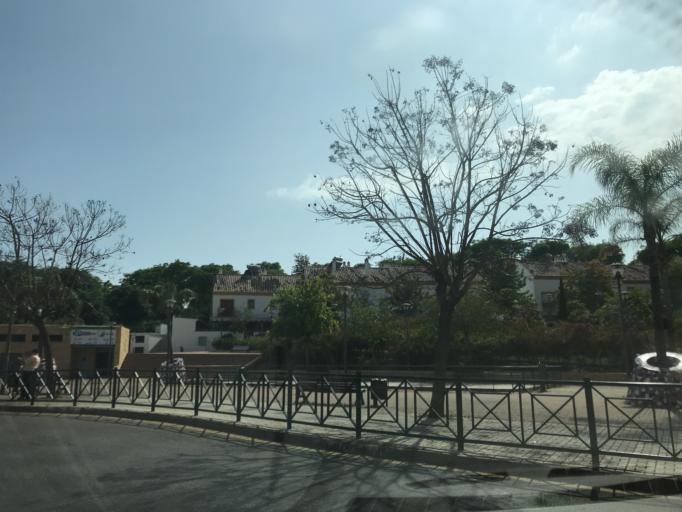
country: ES
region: Andalusia
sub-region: Provincia de Malaga
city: Estepona
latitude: 36.4308
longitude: -5.1490
